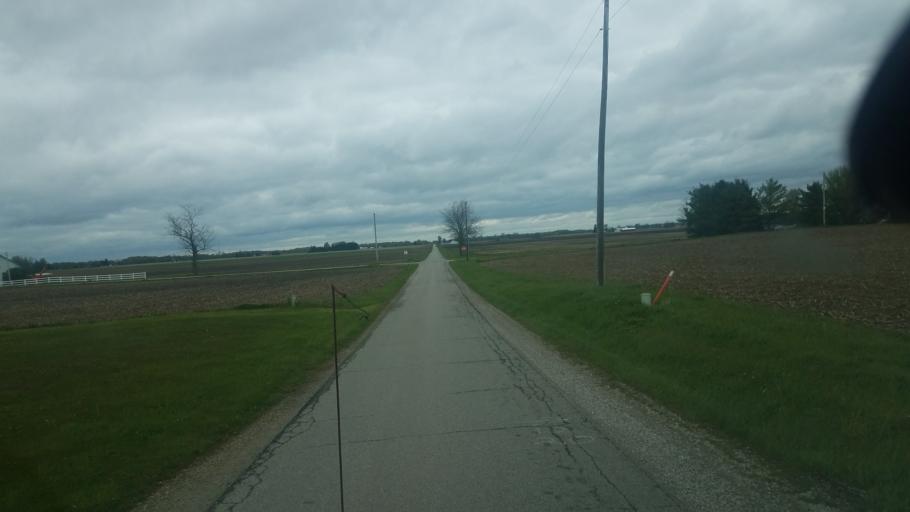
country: US
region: Ohio
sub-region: Crawford County
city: Bucyrus
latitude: 40.7889
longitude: -83.0737
